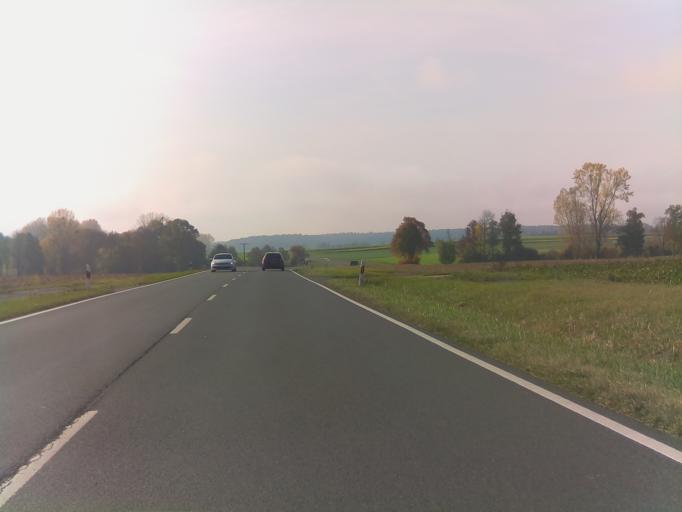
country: DE
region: Bavaria
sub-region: Regierungsbezirk Unterfranken
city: Prichsenstadt
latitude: 49.8257
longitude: 10.3108
